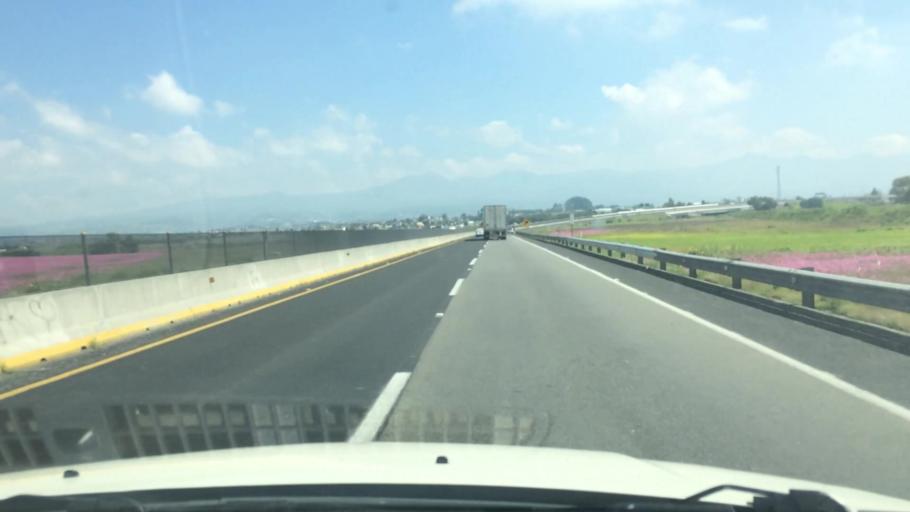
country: MX
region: Mexico
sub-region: Temoaya
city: Llano de la Y
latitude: 19.4084
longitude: -99.6255
